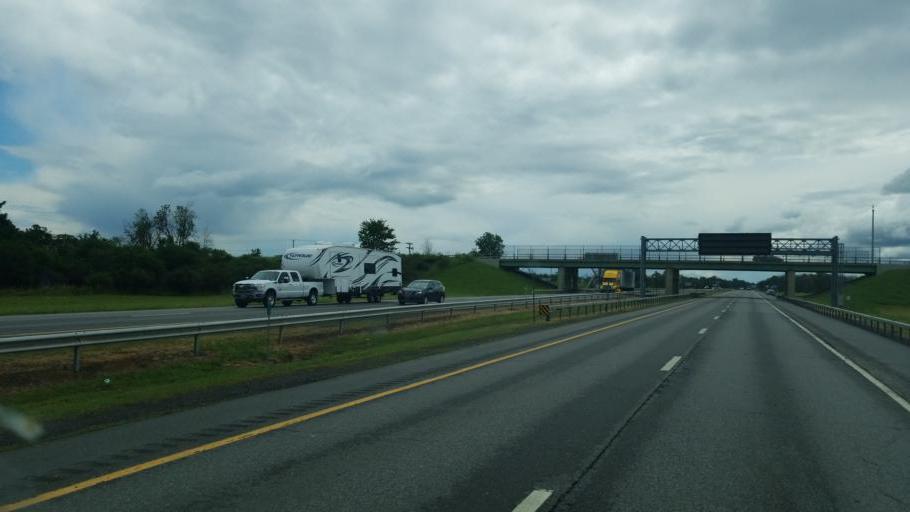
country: US
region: New York
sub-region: Erie County
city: Williamsville
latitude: 42.9506
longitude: -78.7264
